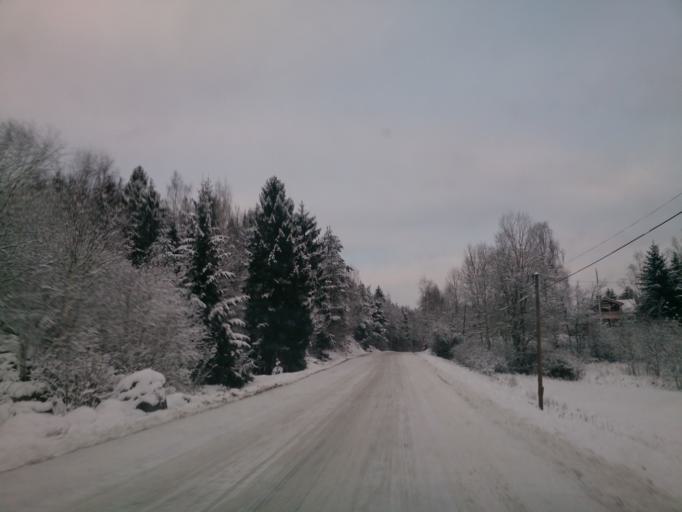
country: SE
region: OEstergoetland
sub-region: Atvidabergs Kommun
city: Atvidaberg
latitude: 58.3067
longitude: 16.0216
